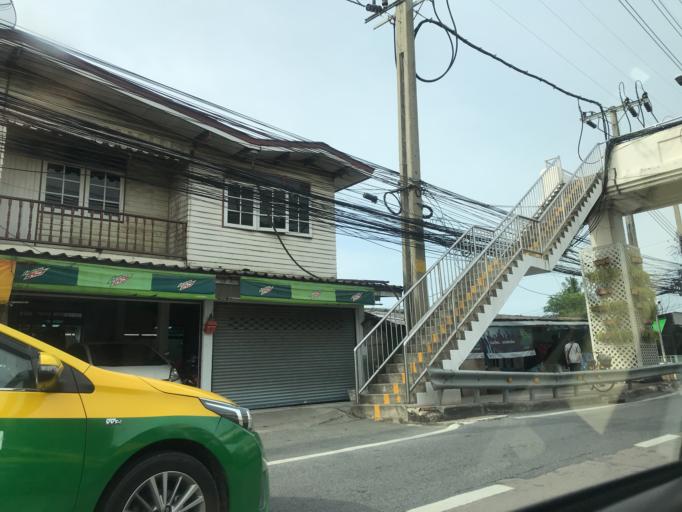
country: TH
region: Bangkok
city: Bueng Kum
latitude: 13.7829
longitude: 100.6729
